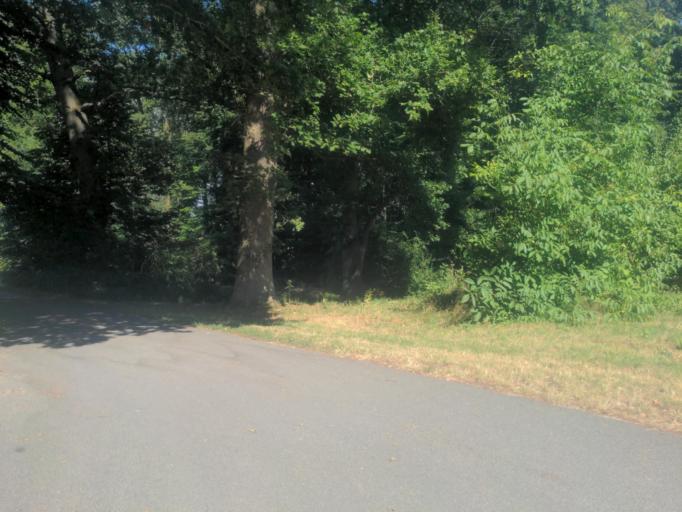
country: DE
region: Lower Saxony
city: Neu Darchau
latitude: 53.2078
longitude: 10.8593
